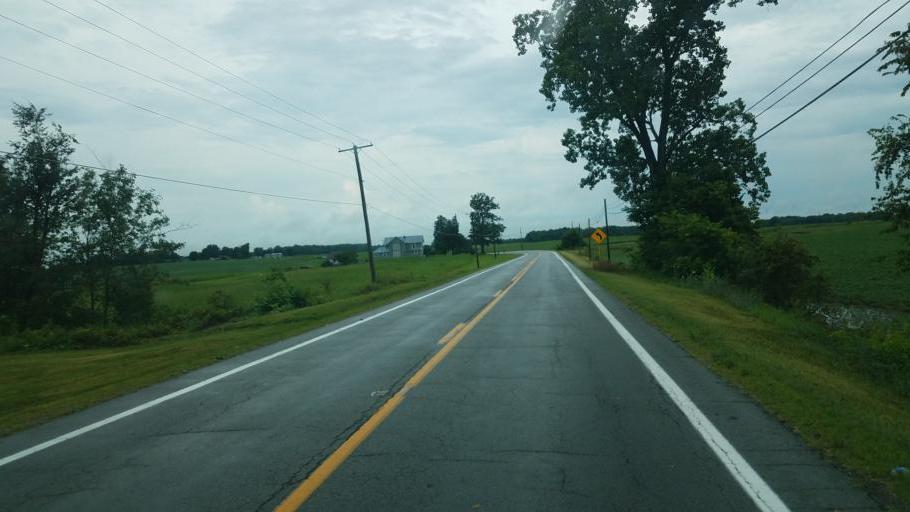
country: US
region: Ohio
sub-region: Marion County
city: Prospect
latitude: 40.5299
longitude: -83.2157
